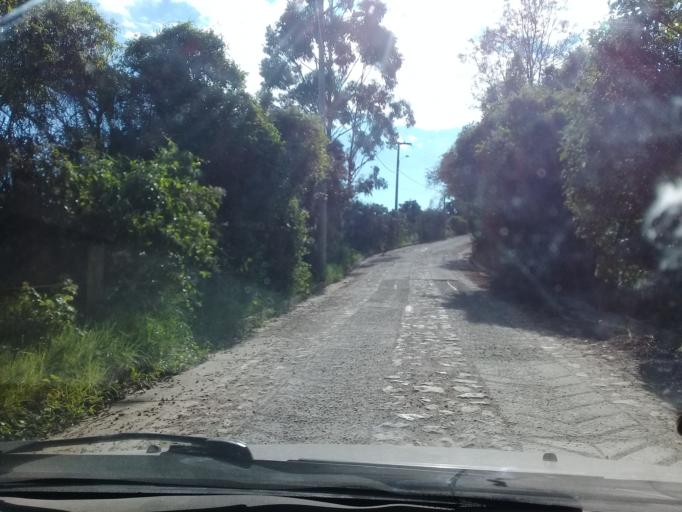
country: CO
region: Cundinamarca
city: Tabio
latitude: 4.9675
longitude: -74.0769
